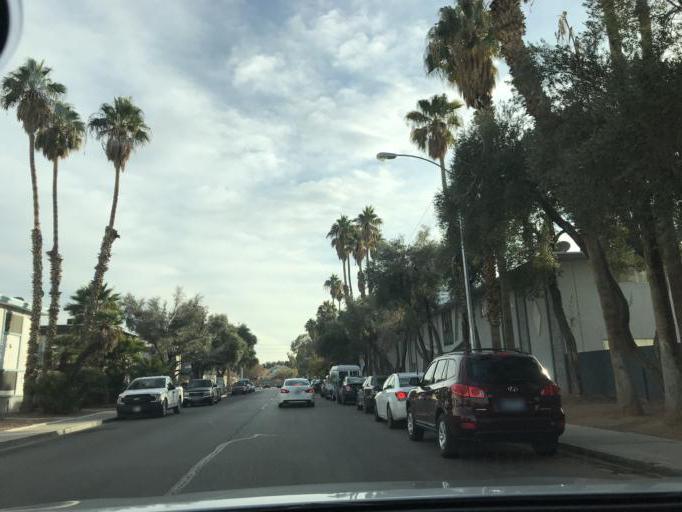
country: US
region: Nevada
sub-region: Clark County
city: Winchester
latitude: 36.1422
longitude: -115.1497
